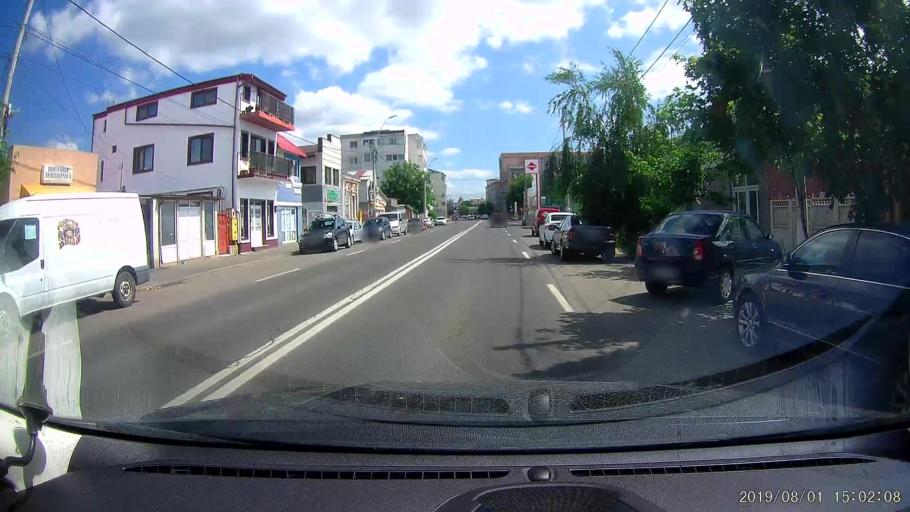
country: RO
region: Braila
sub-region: Municipiul Braila
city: Braila
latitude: 45.2675
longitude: 27.9610
